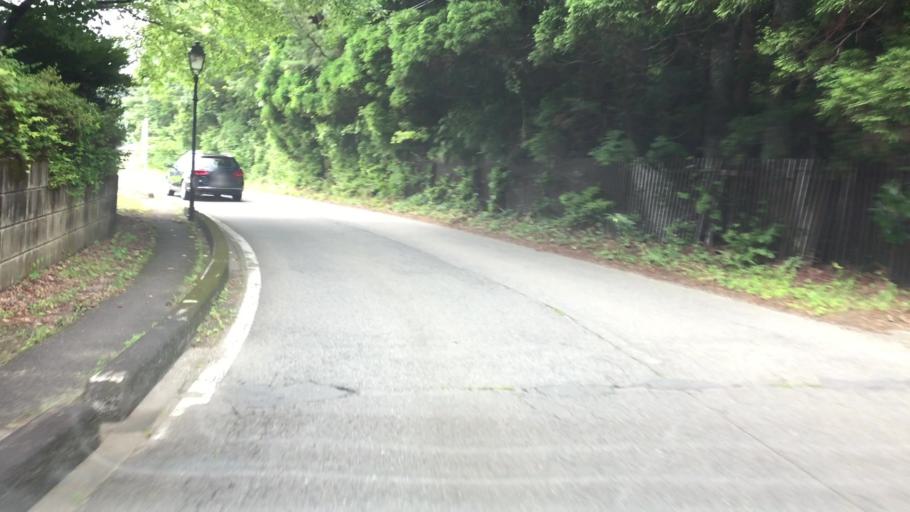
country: JP
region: Tochigi
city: Kuroiso
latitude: 37.0438
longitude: 140.0274
